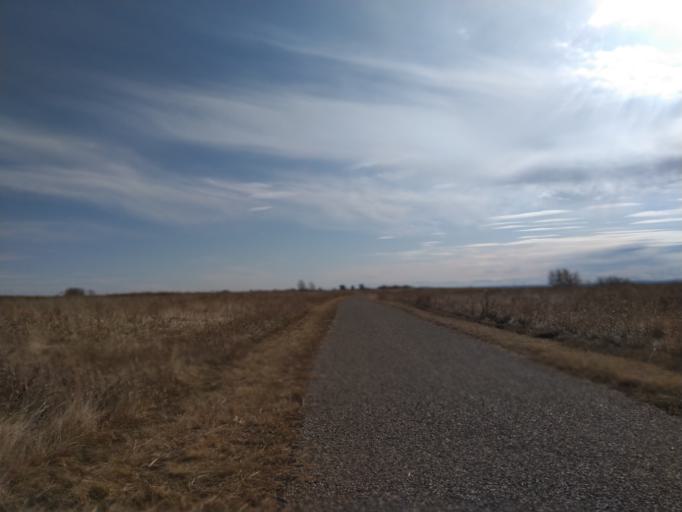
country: CA
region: Alberta
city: Calgary
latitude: 51.1101
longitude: -114.1176
